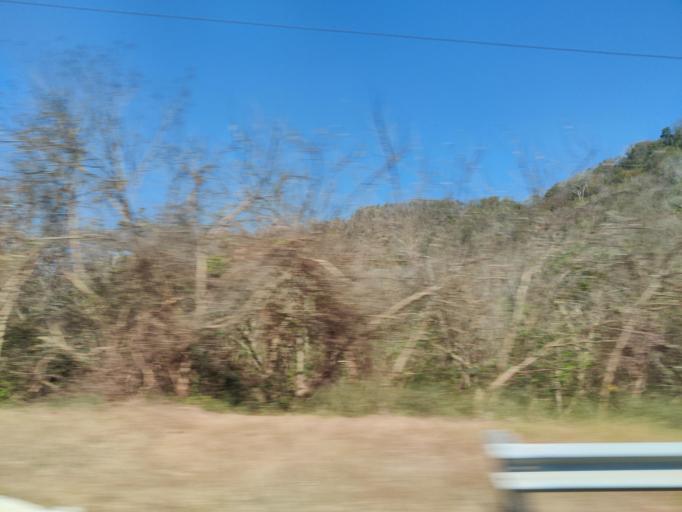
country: CO
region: Atlantico
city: Puerto Colombia
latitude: 10.9573
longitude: -75.0031
